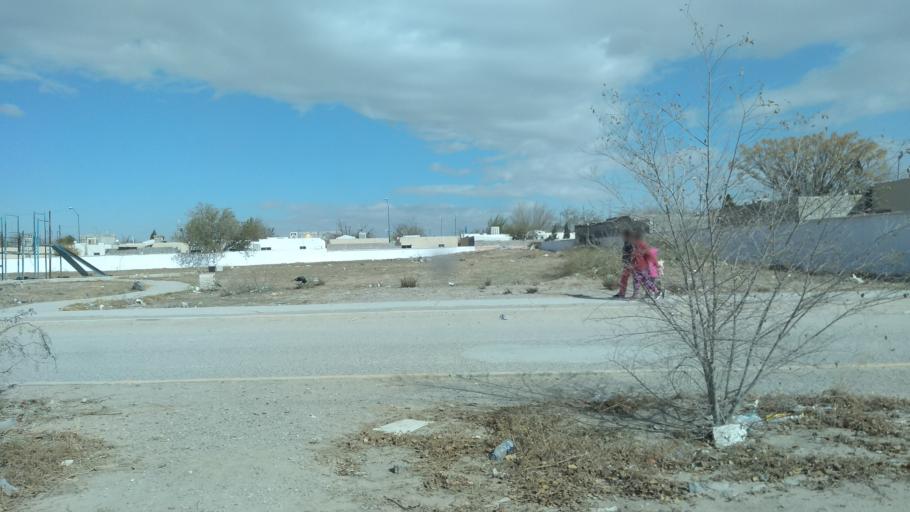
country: US
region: Texas
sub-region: El Paso County
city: San Elizario
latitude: 31.5773
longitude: -106.3456
